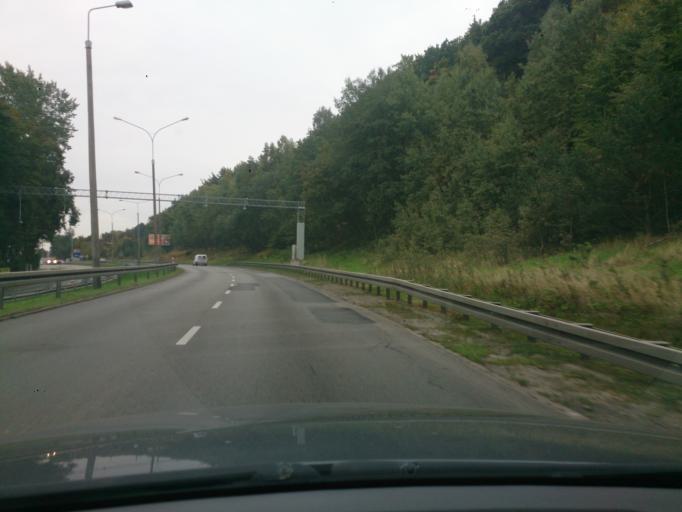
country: PL
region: Pomeranian Voivodeship
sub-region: Powiat wejherowski
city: Rumia
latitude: 54.5546
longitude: 18.4119
